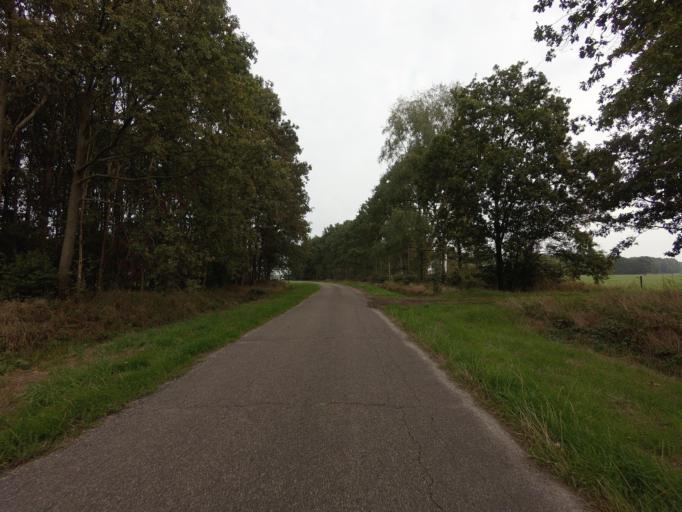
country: NL
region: Drenthe
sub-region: Gemeente Westerveld
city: Dwingeloo
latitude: 52.8608
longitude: 6.4118
